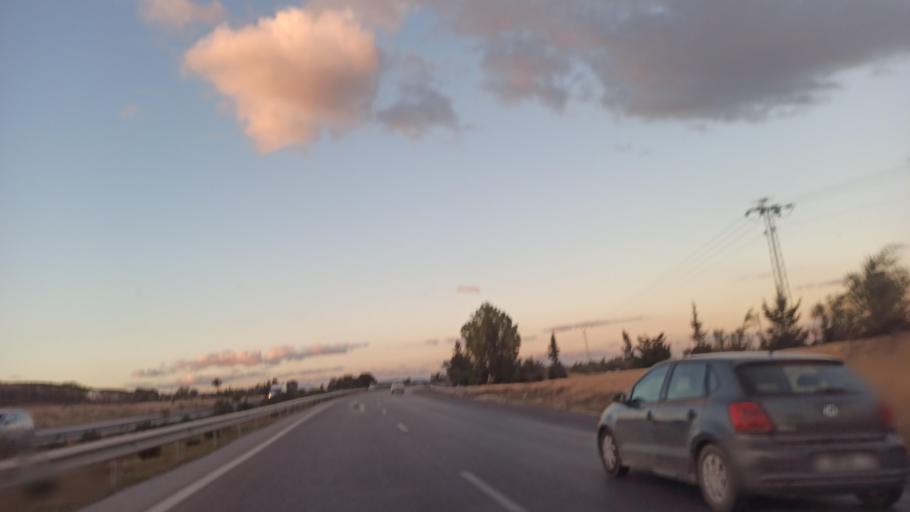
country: TN
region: Susah
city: Harqalah
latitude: 36.2308
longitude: 10.4131
